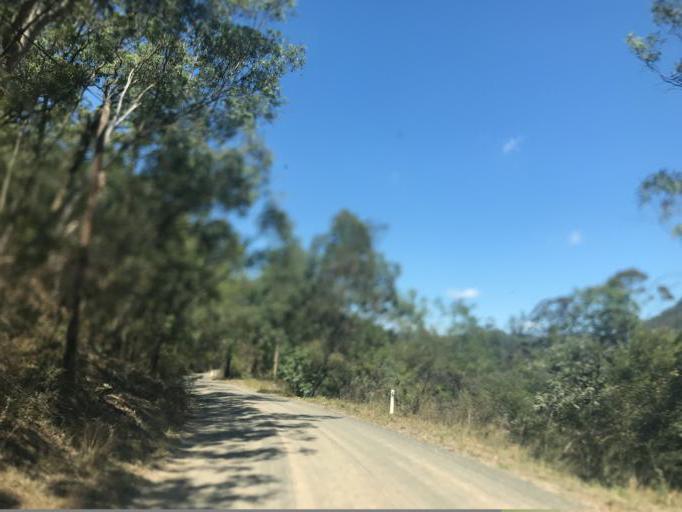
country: AU
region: New South Wales
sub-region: Hornsby Shire
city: Glenorie
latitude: -33.2617
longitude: 150.9718
